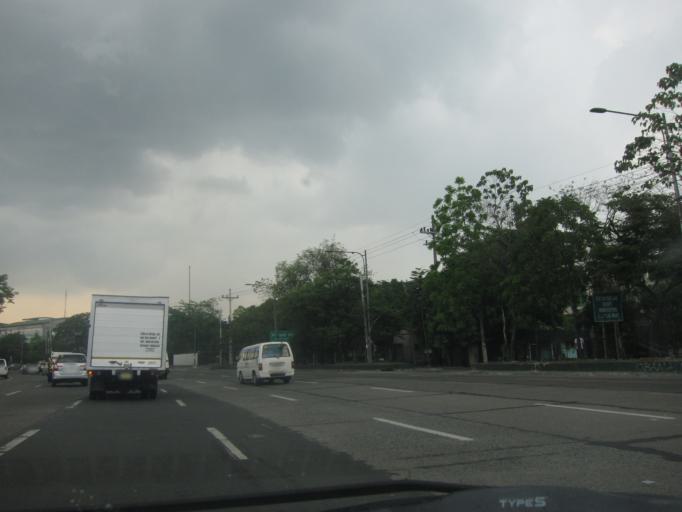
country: PH
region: Metro Manila
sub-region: Quezon City
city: Quezon City
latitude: 14.6542
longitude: 121.0498
